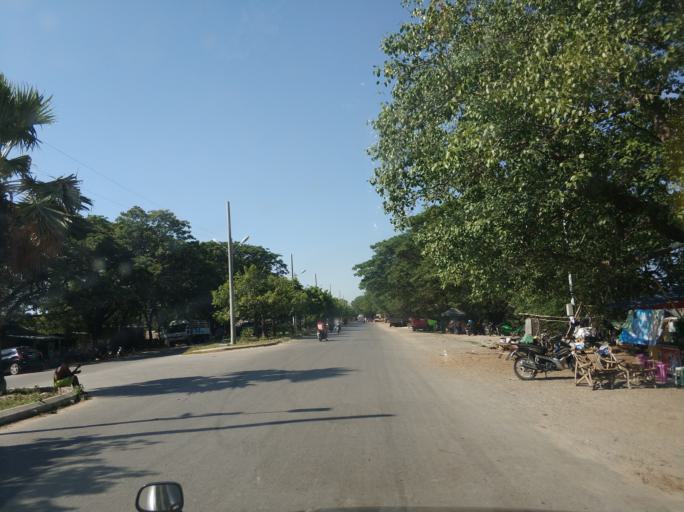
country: MM
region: Mandalay
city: Mandalay
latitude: 21.9668
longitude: 96.0562
